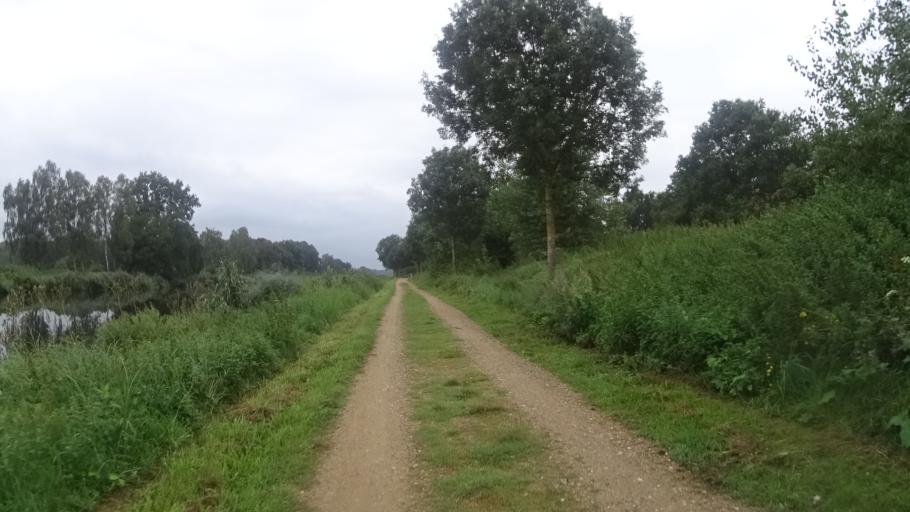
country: DE
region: Schleswig-Holstein
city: Witzeeze
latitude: 53.4504
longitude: 10.6221
